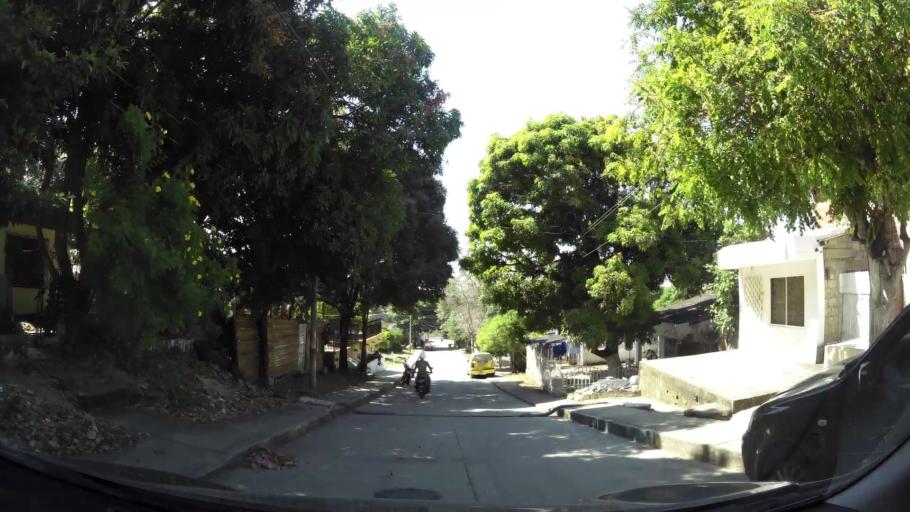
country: CO
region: Bolivar
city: Cartagena
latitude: 10.3906
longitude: -75.5109
